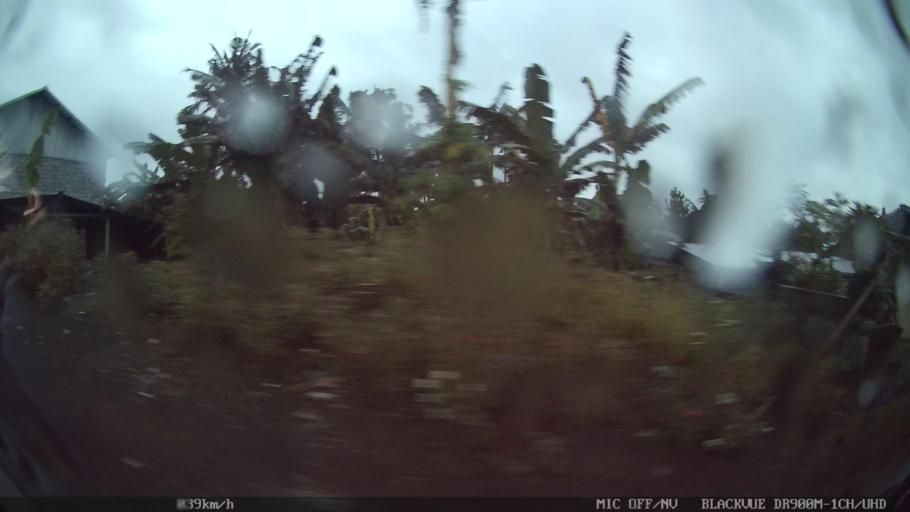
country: ID
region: Bali
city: Banjar Sedang
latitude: -8.5607
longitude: 115.2514
